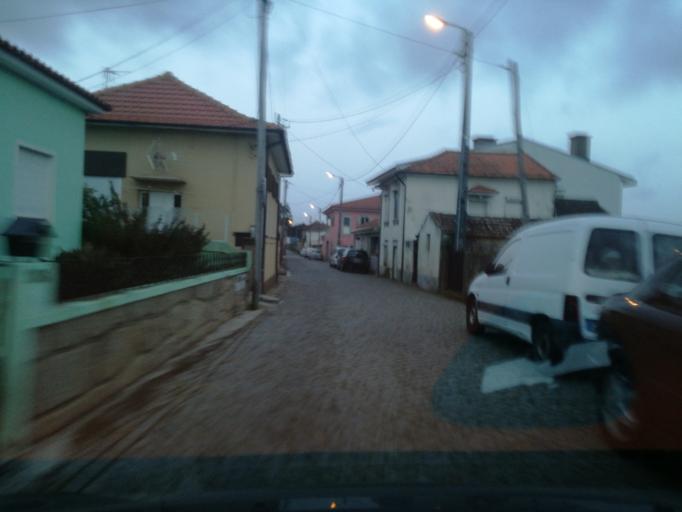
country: PT
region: Porto
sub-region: Maia
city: Gemunde
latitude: 41.2685
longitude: -8.6571
